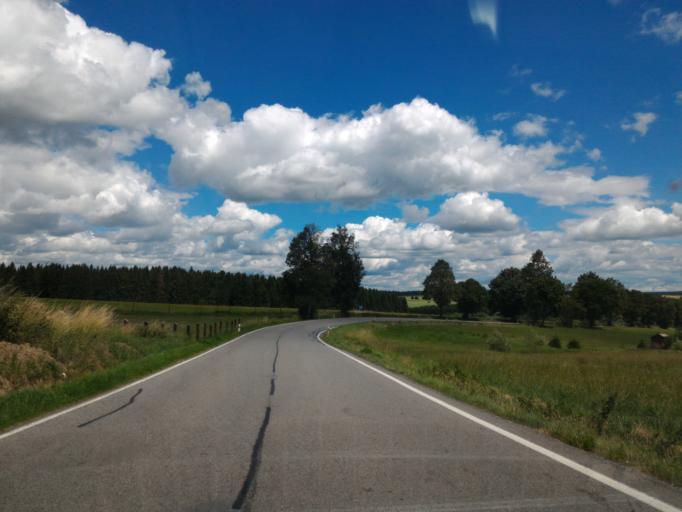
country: CZ
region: Vysocina
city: Velky Beranov
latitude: 49.4289
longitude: 15.7038
